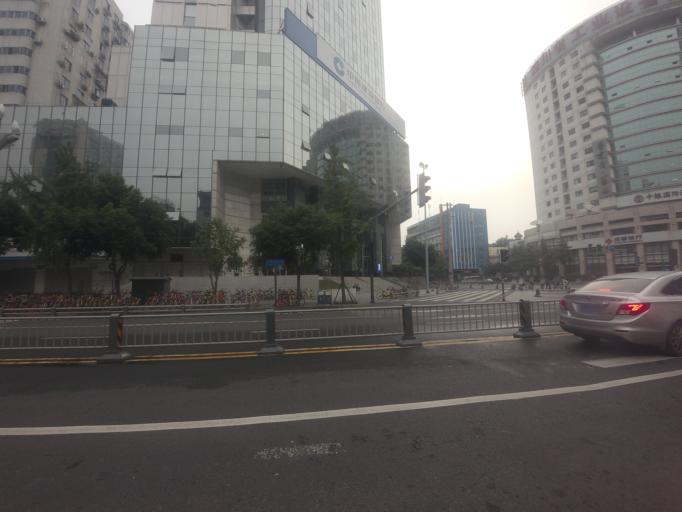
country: CN
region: Sichuan
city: Chengdu
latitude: 30.6747
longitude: 104.0651
